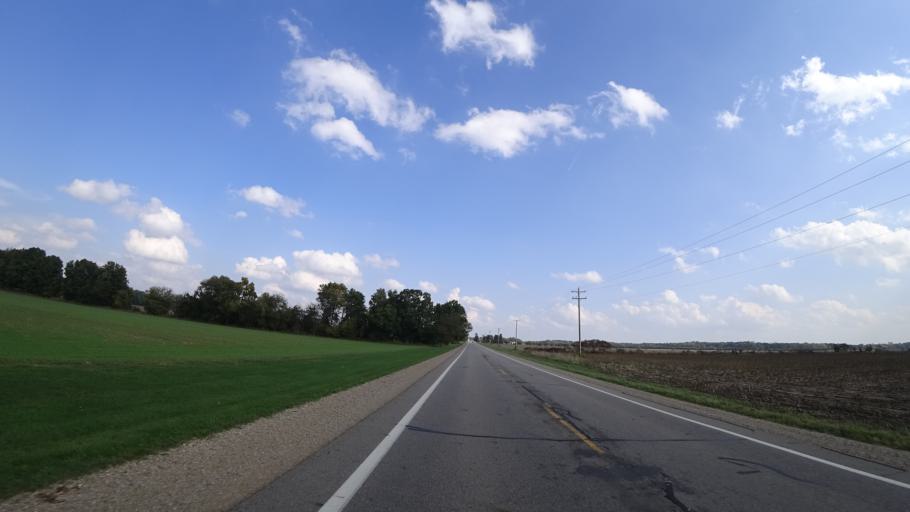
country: US
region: Michigan
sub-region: Saint Joseph County
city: Centreville
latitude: 42.0062
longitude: -85.4993
